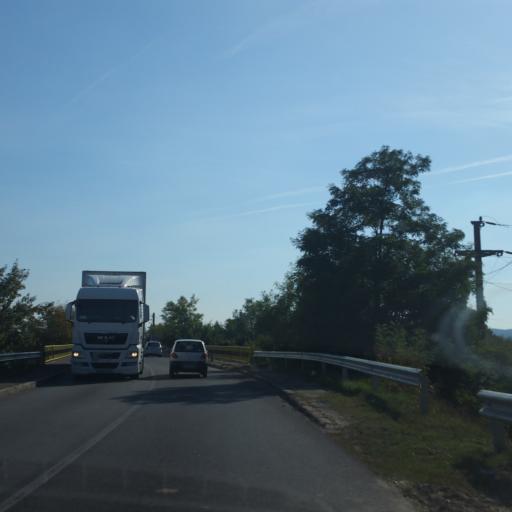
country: RO
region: Arges
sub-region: Municipiul Curtea de Arges
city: Curtea de Arges
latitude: 45.1046
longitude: 24.6692
